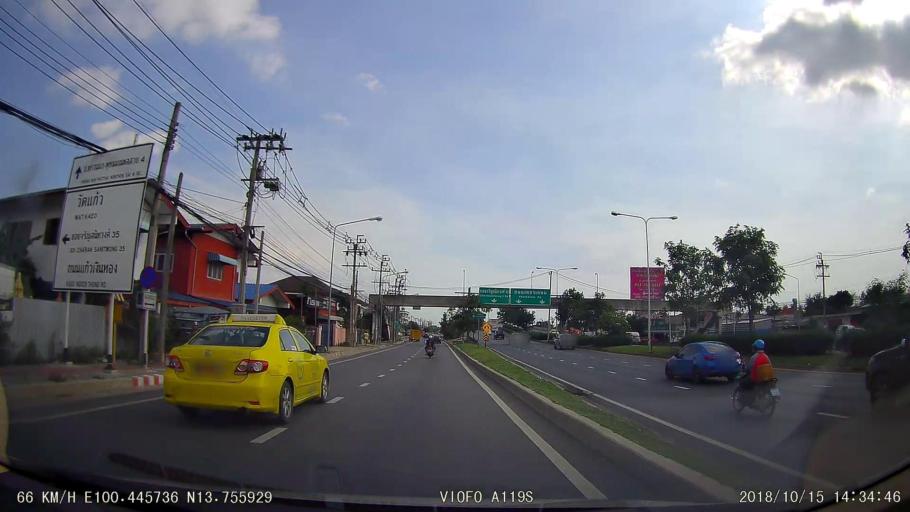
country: TH
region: Bangkok
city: Taling Chan
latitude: 13.7556
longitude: 100.4458
